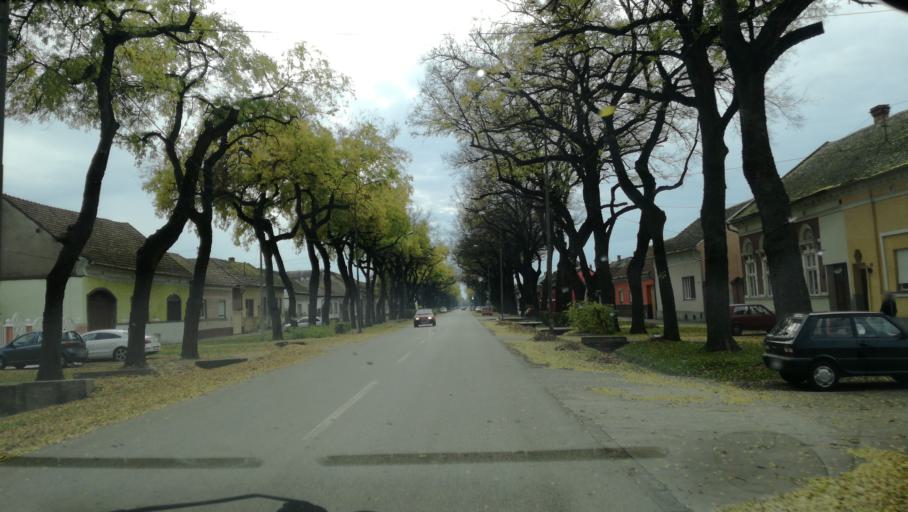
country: RS
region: Autonomna Pokrajina Vojvodina
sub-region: Severnobanatski Okrug
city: Kikinda
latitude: 45.8388
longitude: 20.4801
